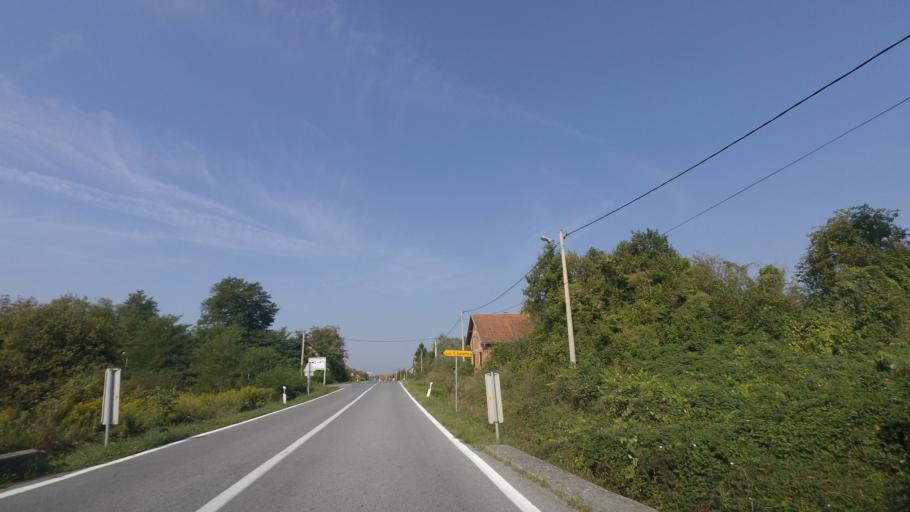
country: HR
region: Bjelovarsko-Bilogorska
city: Sirac
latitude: 45.4725
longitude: 17.3059
